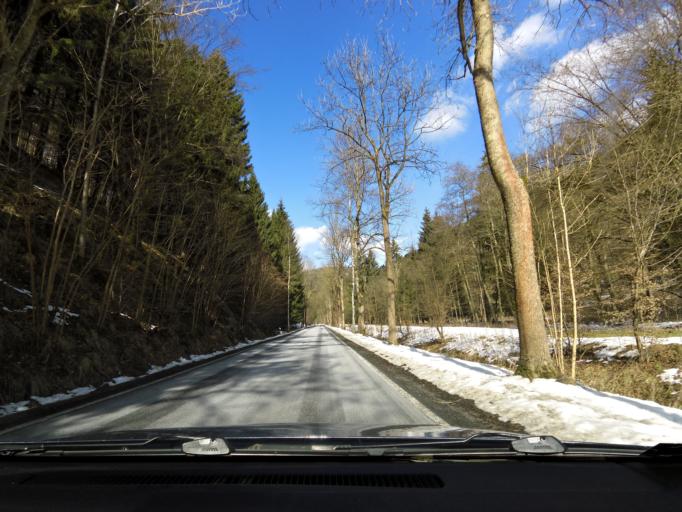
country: DE
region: Lower Saxony
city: Sankt Andreasberg
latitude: 51.6671
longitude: 10.5064
